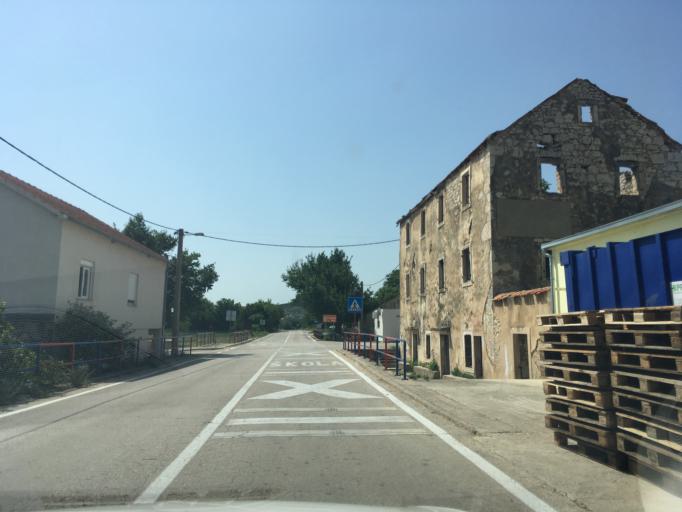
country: HR
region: Zadarska
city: Benkovac
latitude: 43.9615
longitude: 15.7662
